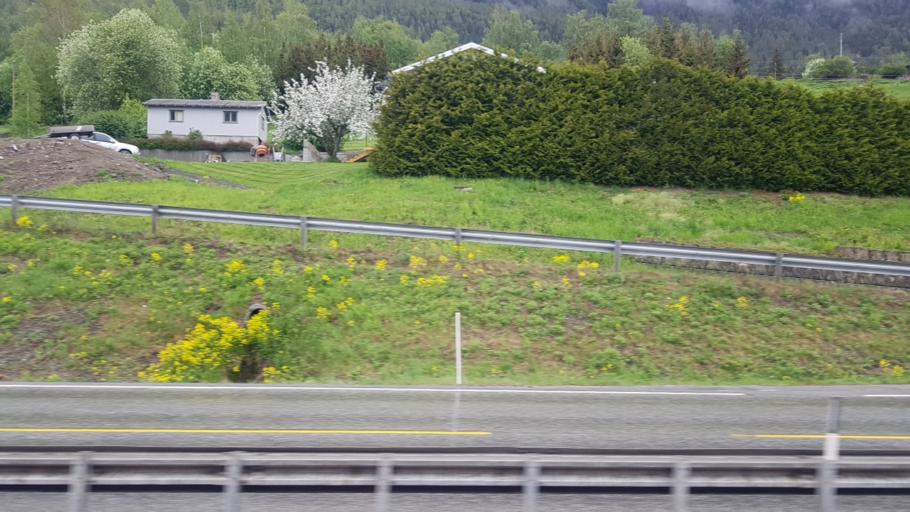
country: NO
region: Oppland
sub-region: Nord-Fron
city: Vinstra
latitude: 61.6664
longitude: 9.6706
